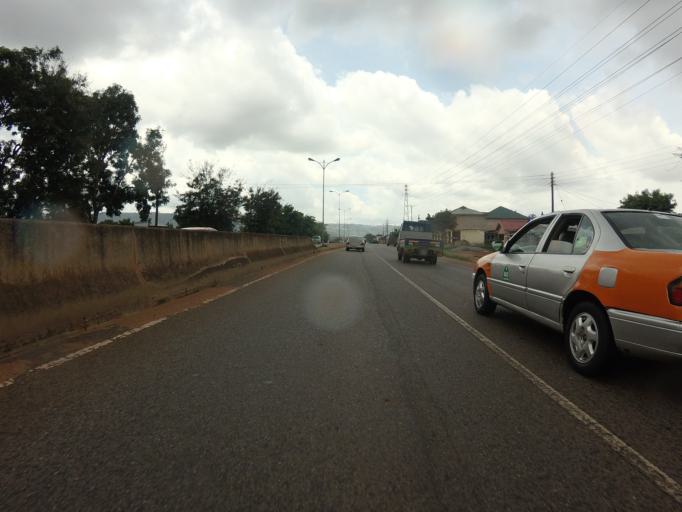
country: GH
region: Greater Accra
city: Medina Estates
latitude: 5.7487
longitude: -0.1776
